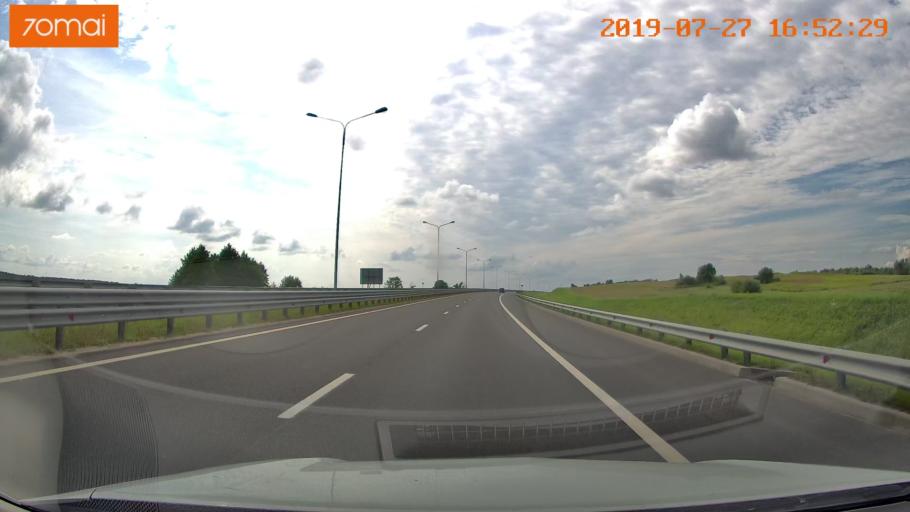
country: RU
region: Kaliningrad
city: Gvardeysk
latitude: 54.6836
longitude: 20.8584
